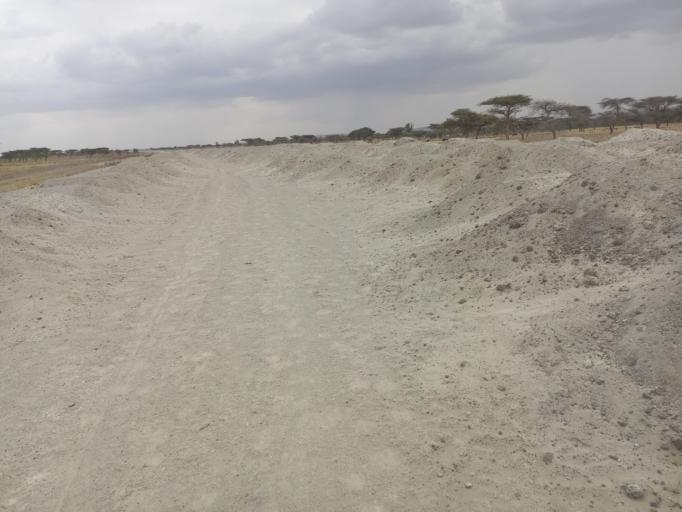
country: ET
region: Oromiya
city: Ziway
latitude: 7.8943
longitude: 38.6754
